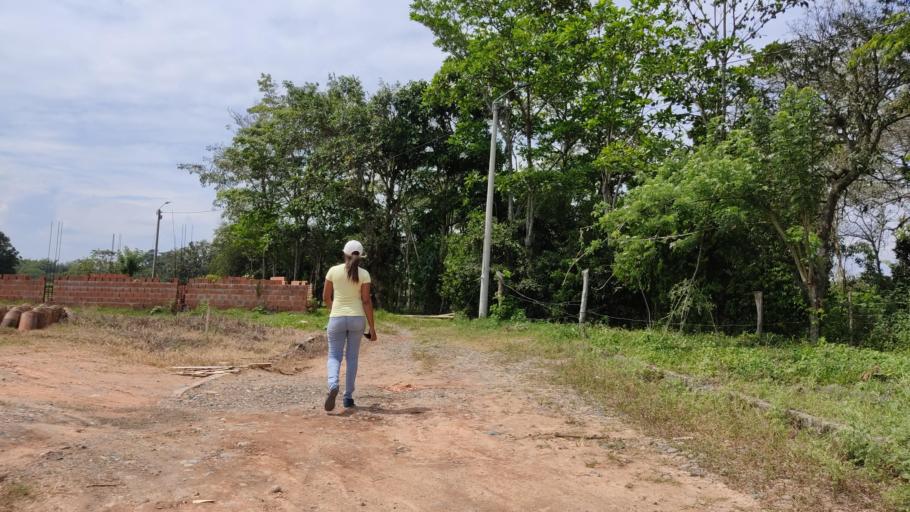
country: CO
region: Cauca
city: Buenos Aires
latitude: 3.1256
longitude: -76.5908
